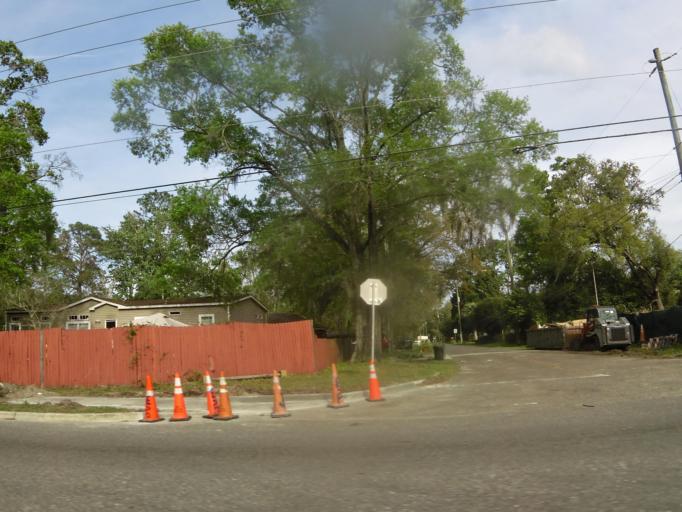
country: US
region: Florida
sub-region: Clay County
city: Bellair-Meadowbrook Terrace
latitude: 30.2525
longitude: -81.7858
